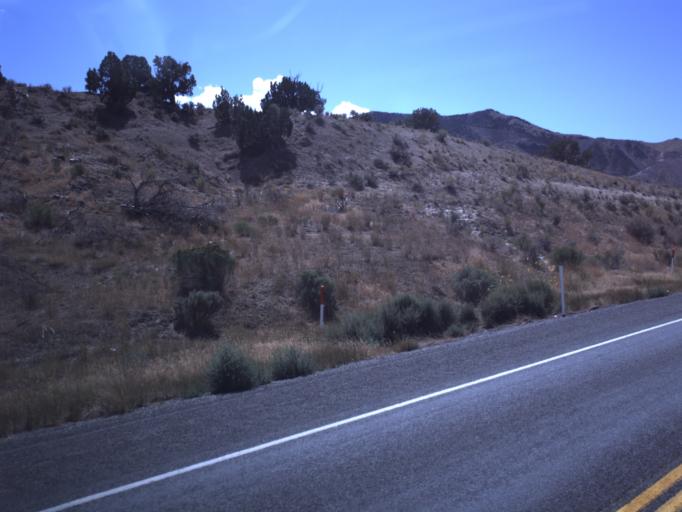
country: US
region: Utah
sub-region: Juab County
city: Nephi
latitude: 39.5717
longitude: -112.1887
